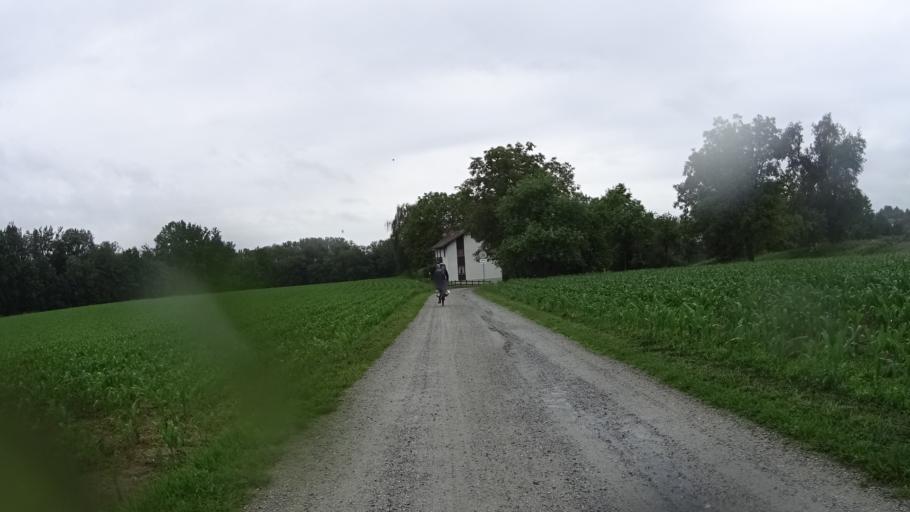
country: AT
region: Upper Austria
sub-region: Politischer Bezirk Scharding
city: Scharding
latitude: 48.4753
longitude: 13.4313
